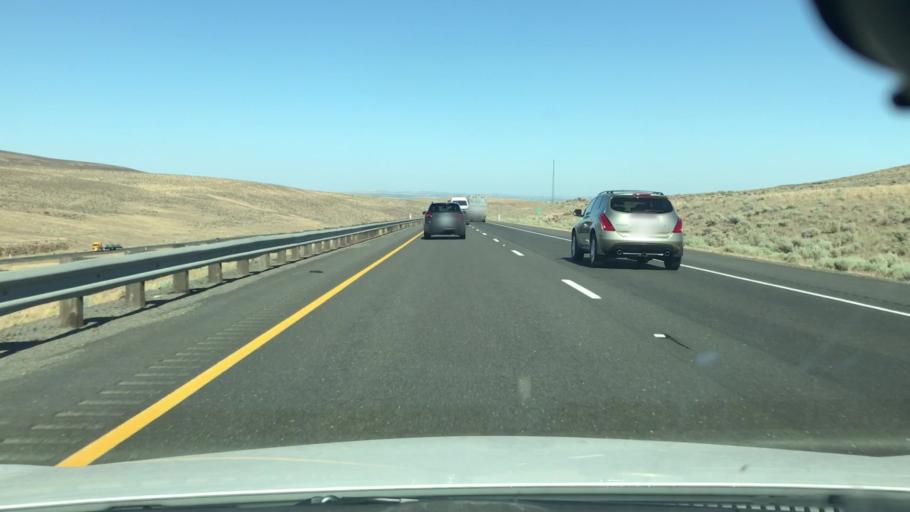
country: US
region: Washington
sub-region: Grant County
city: Mattawa
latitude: 46.9450
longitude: -120.0997
